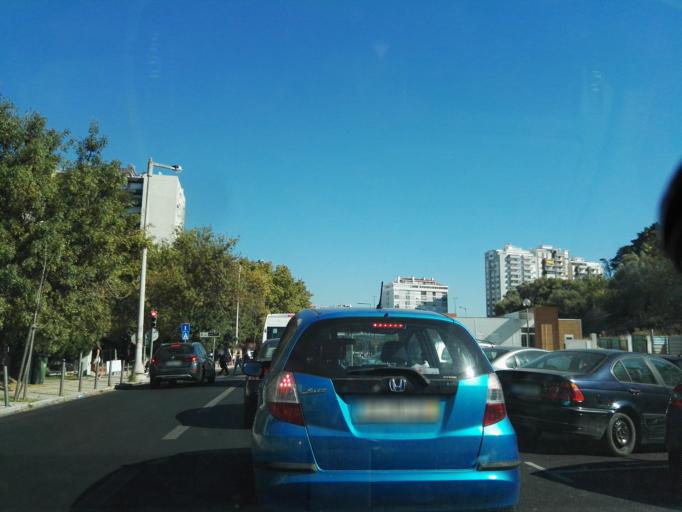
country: PT
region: Lisbon
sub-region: Odivelas
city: Pontinha
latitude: 38.7482
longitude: -9.1923
